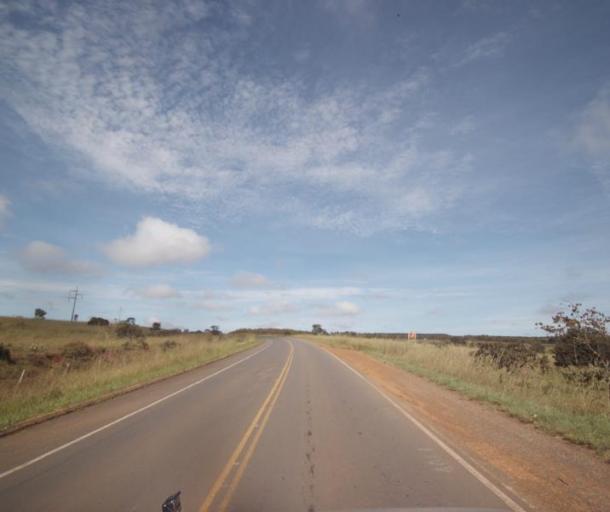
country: BR
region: Goias
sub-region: Pirenopolis
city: Pirenopolis
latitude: -16.0285
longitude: -48.8486
